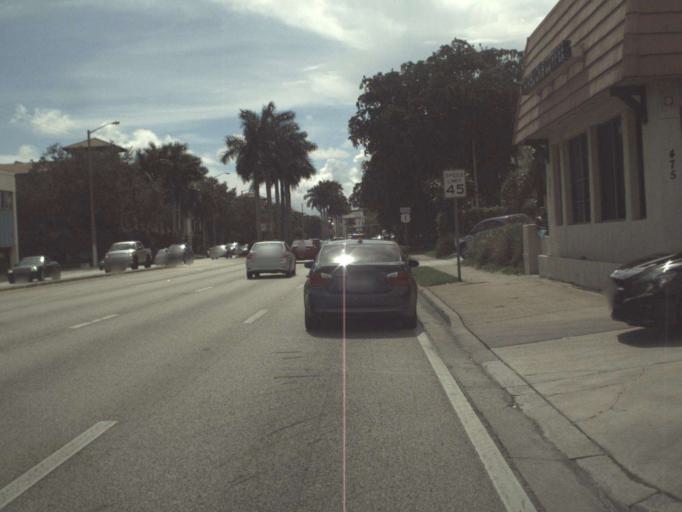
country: US
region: Florida
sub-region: Miami-Dade County
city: Coral Gables
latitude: 25.7257
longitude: -80.2629
